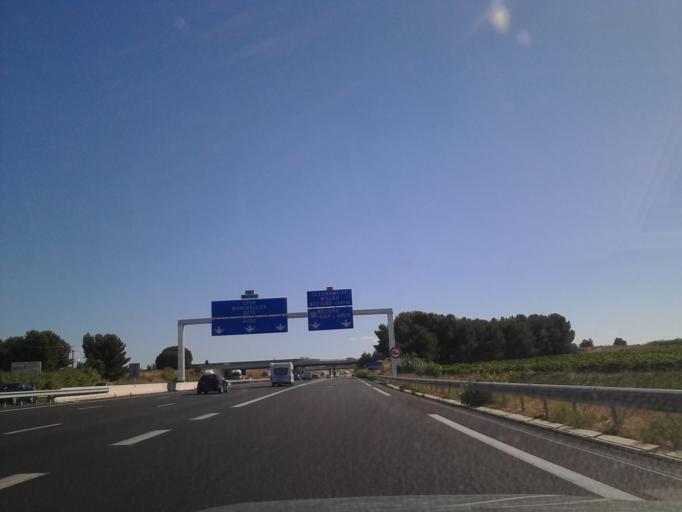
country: FR
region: Languedoc-Roussillon
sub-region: Departement de l'Herault
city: Villeneuve-les-Beziers
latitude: 43.3316
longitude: 3.2815
